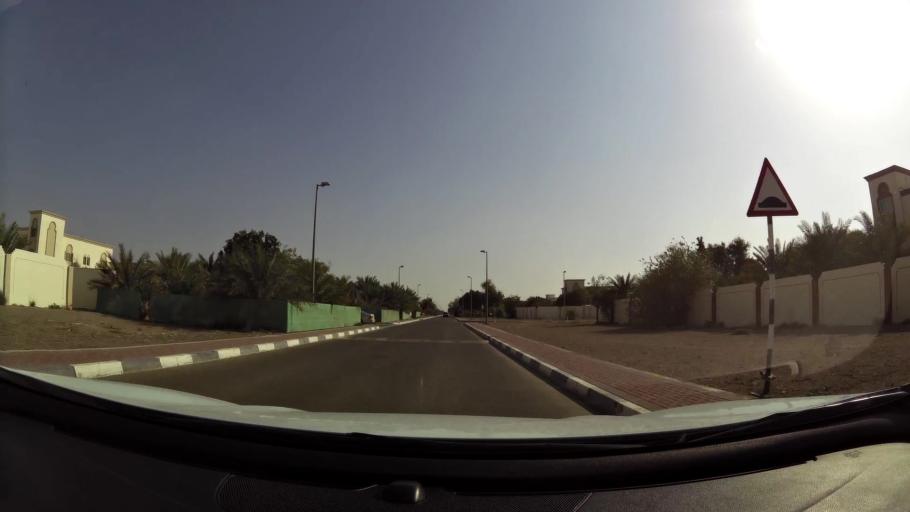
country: AE
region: Abu Dhabi
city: Al Ain
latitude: 24.0786
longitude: 55.8630
